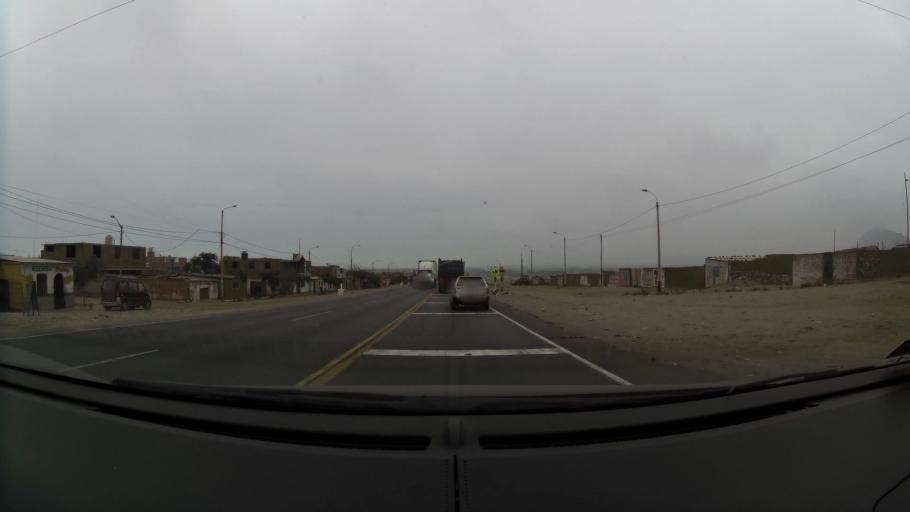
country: PE
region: La Libertad
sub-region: Provincia de Trujillo
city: Moche
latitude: -8.1820
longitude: -78.9878
